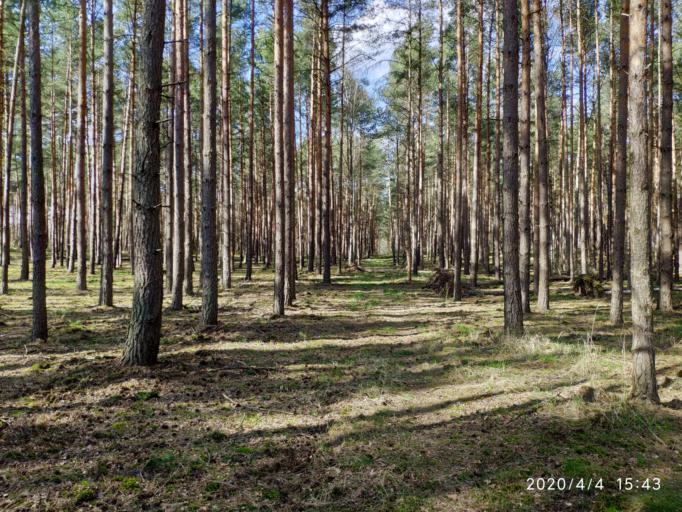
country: PL
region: Lubusz
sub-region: Powiat zielonogorski
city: Swidnica
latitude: 51.8949
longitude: 15.2924
